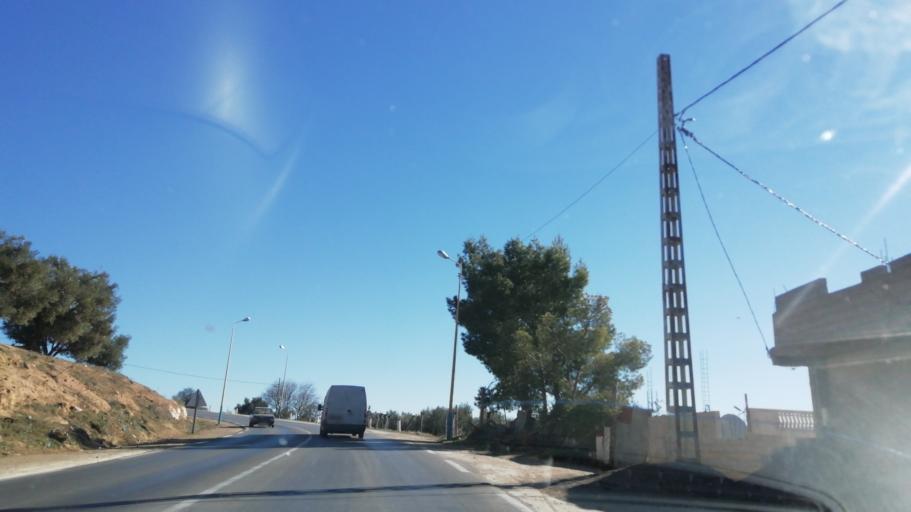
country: DZ
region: Tlemcen
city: Sebdou
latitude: 34.6812
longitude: -1.3153
